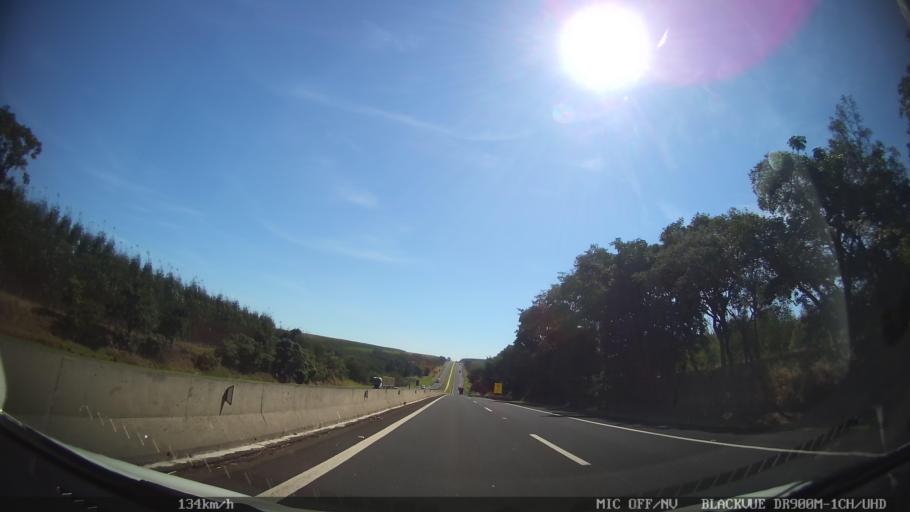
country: BR
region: Sao Paulo
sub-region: Sao Simao
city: Sao Simao
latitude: -21.5809
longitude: -47.6276
